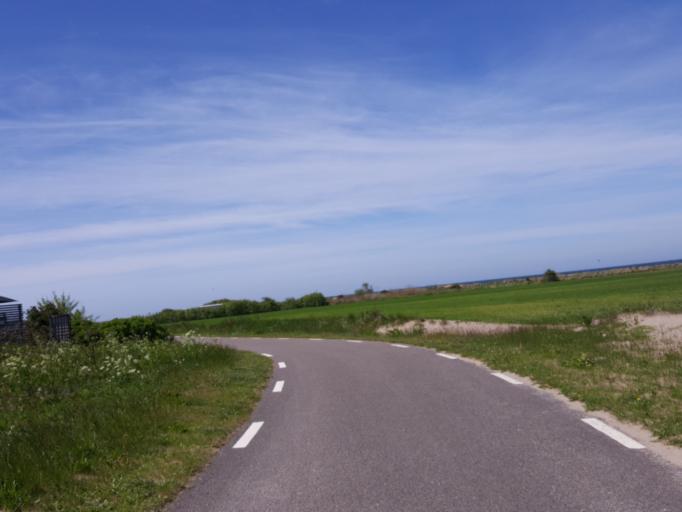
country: SE
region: Halland
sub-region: Falkenbergs Kommun
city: Falkenberg
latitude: 56.8591
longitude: 12.5521
